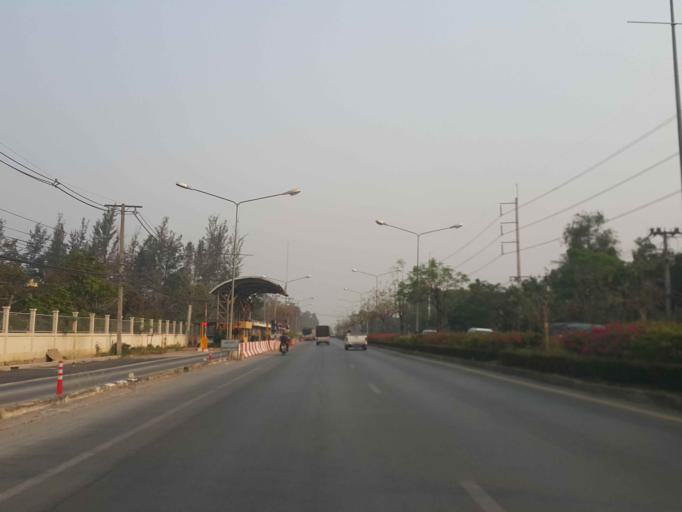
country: TH
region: Chiang Mai
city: San Sai
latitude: 18.9083
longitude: 99.0018
